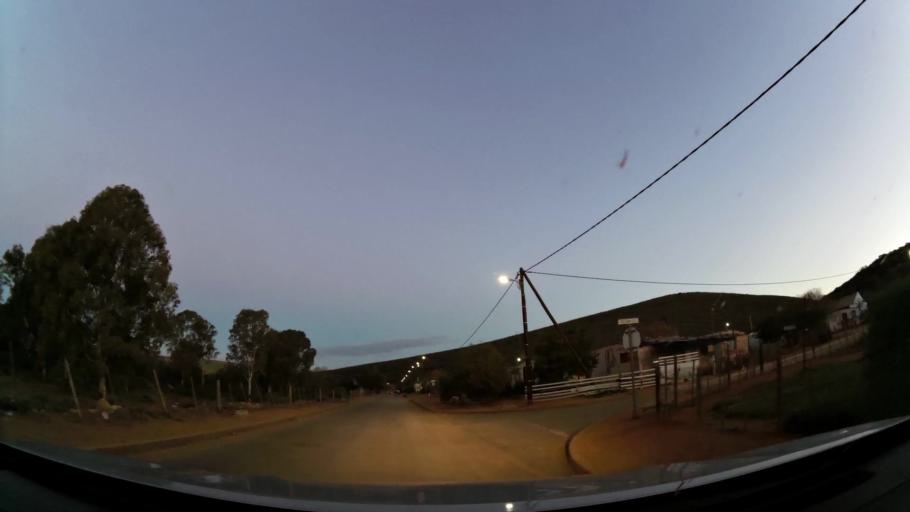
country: ZA
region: Western Cape
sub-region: Eden District Municipality
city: Riversdale
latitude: -34.1056
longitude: 21.2748
